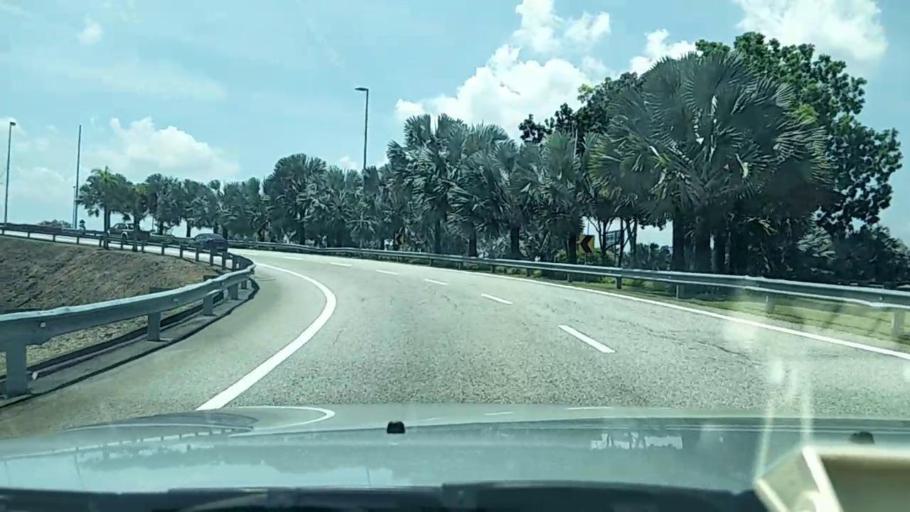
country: MY
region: Putrajaya
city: Putrajaya
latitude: 2.9267
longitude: 101.6672
